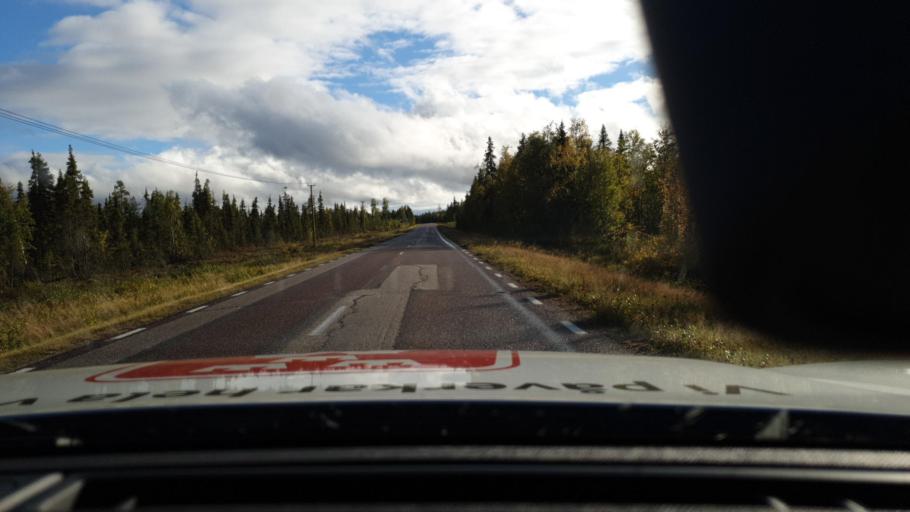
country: SE
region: Norrbotten
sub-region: Overkalix Kommun
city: OEverkalix
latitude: 66.8711
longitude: 22.7585
